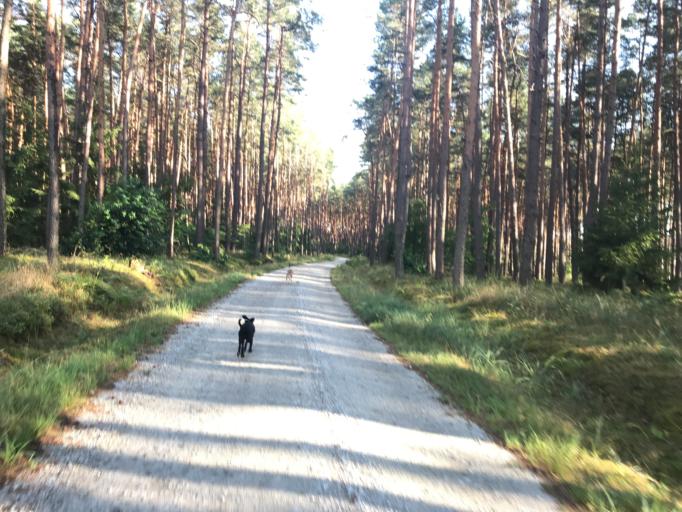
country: PL
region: Greater Poland Voivodeship
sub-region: Powiat szamotulski
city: Obrzycko
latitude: 52.7349
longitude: 16.5885
